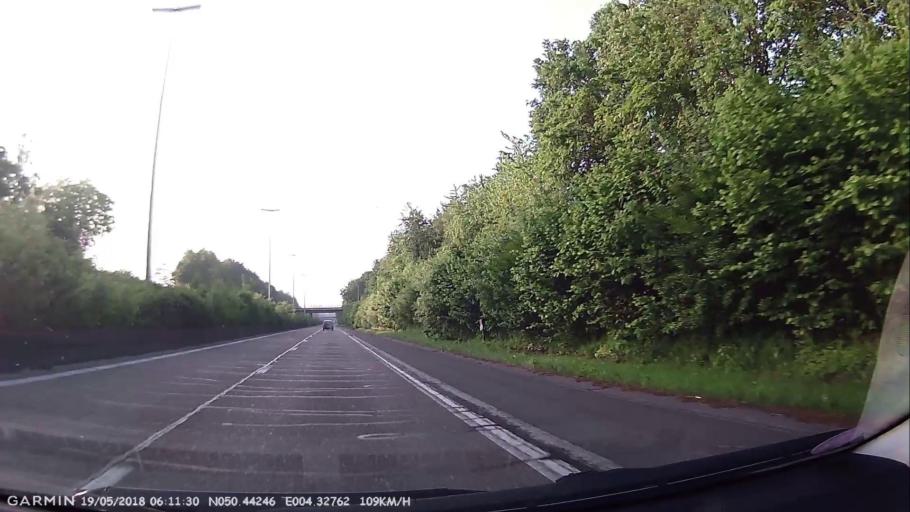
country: BE
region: Wallonia
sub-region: Province du Hainaut
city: Courcelles
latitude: 50.4422
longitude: 4.3280
